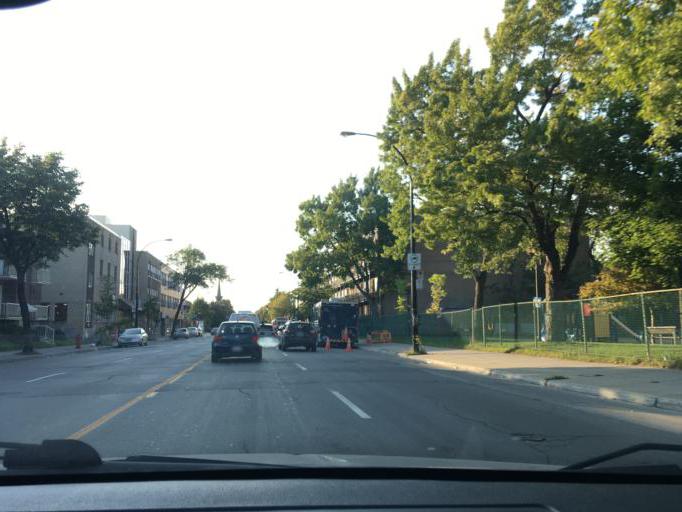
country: CA
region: Quebec
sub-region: Montreal
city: Montreal
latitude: 45.5457
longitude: -73.6020
